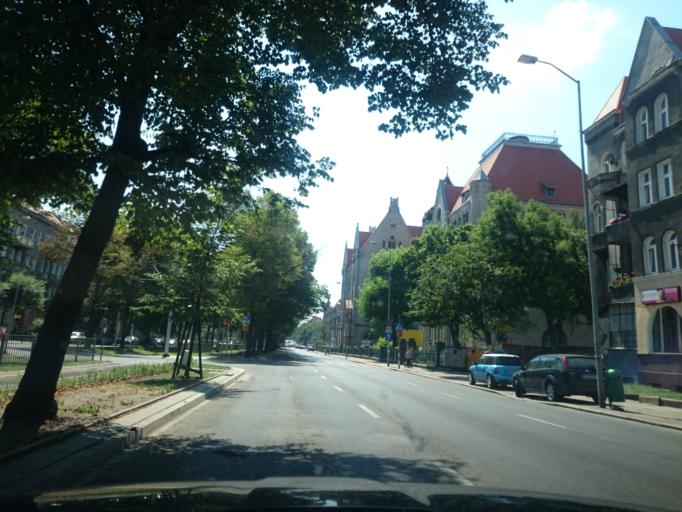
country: PL
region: West Pomeranian Voivodeship
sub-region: Szczecin
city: Szczecin
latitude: 53.4298
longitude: 14.5379
